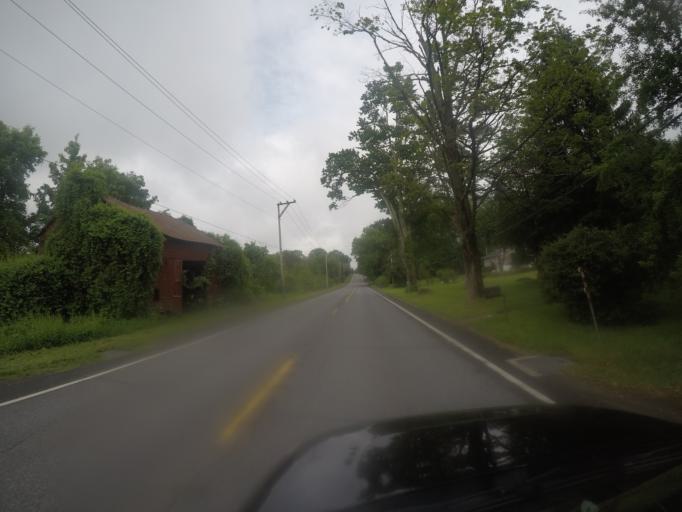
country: US
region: New York
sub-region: Ulster County
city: Shokan
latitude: 41.9731
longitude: -74.2178
